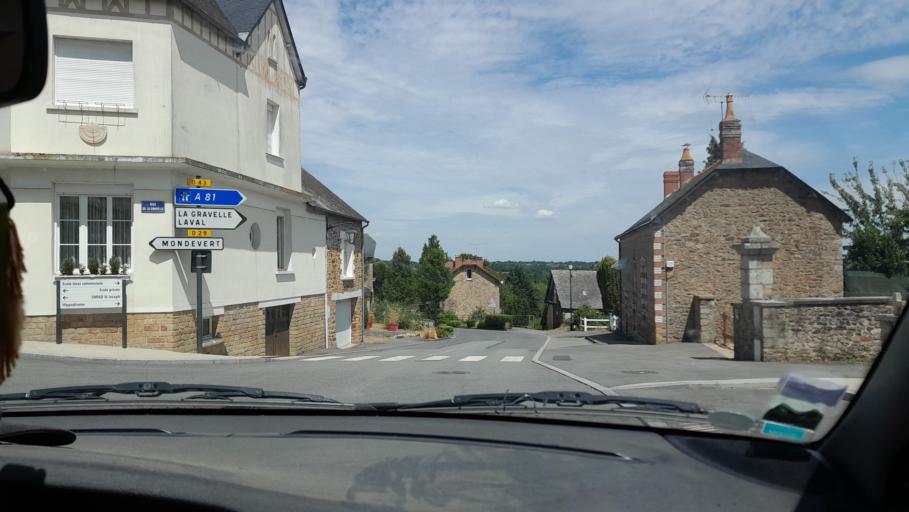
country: FR
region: Brittany
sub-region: Departement d'Ille-et-Vilaine
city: Le Pertre
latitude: 48.0350
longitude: -1.0367
